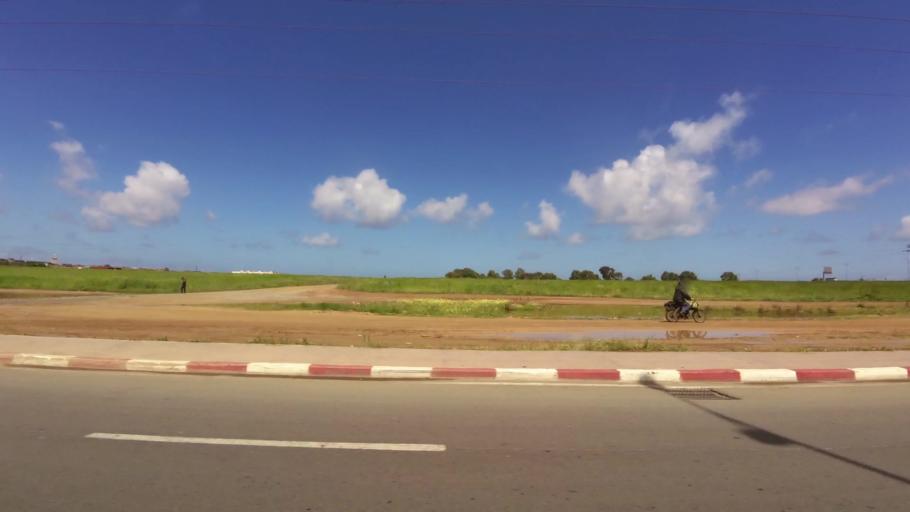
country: MA
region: Grand Casablanca
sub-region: Nouaceur
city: Dar Bouazza
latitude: 33.5393
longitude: -7.7167
